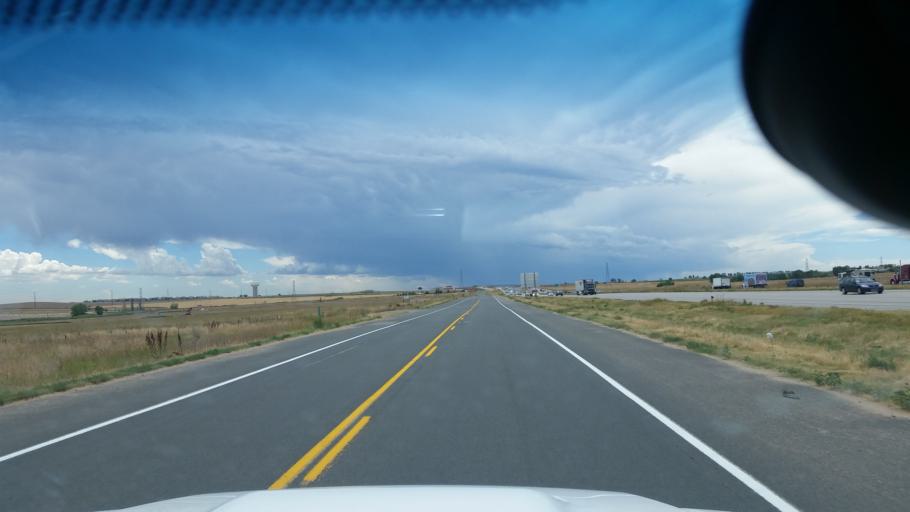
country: US
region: Colorado
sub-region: Weld County
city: Dacono
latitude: 40.0683
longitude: -104.9801
